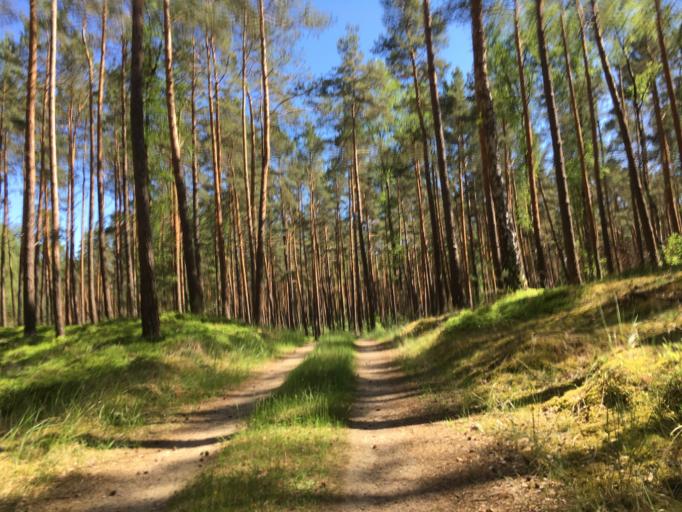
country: DE
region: Brandenburg
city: Joachimsthal
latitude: 52.9623
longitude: 13.6771
